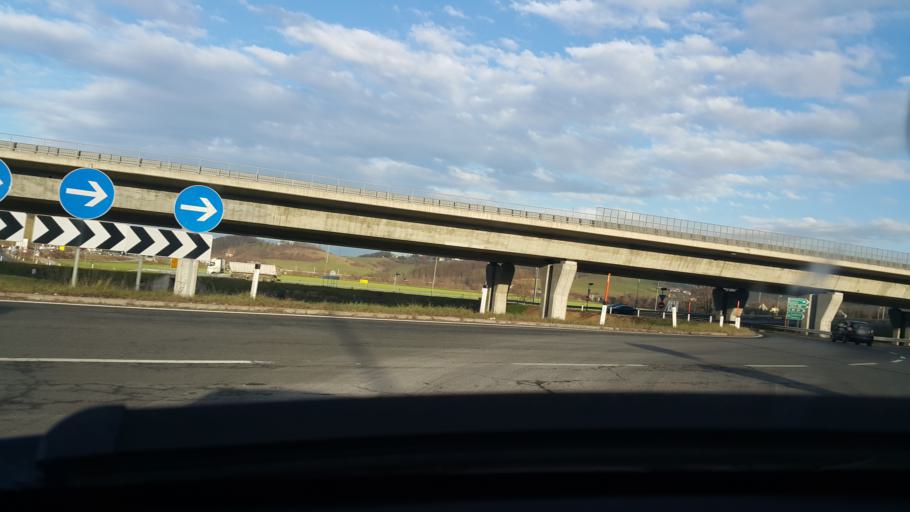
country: SI
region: Pesnica
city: Pesnica pri Mariboru
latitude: 46.5957
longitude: 15.6705
